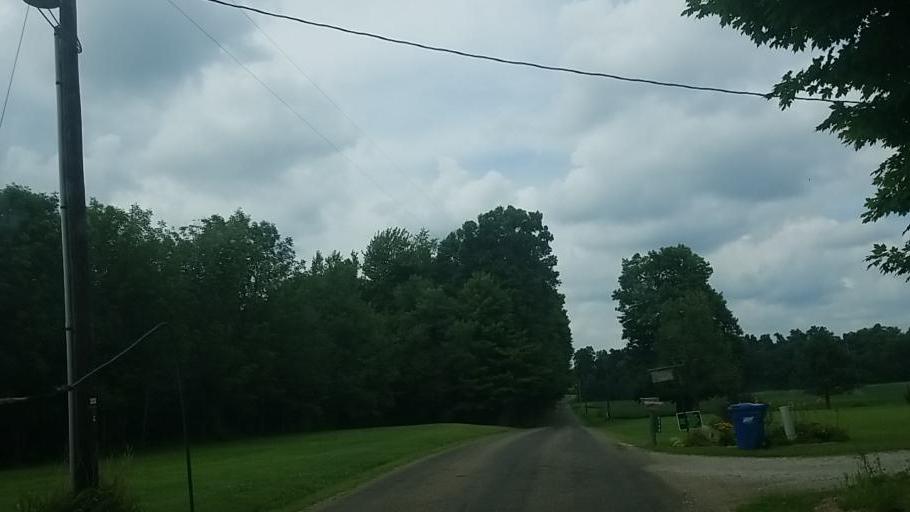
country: US
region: Ohio
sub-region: Knox County
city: Gambier
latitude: 40.3297
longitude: -82.4301
